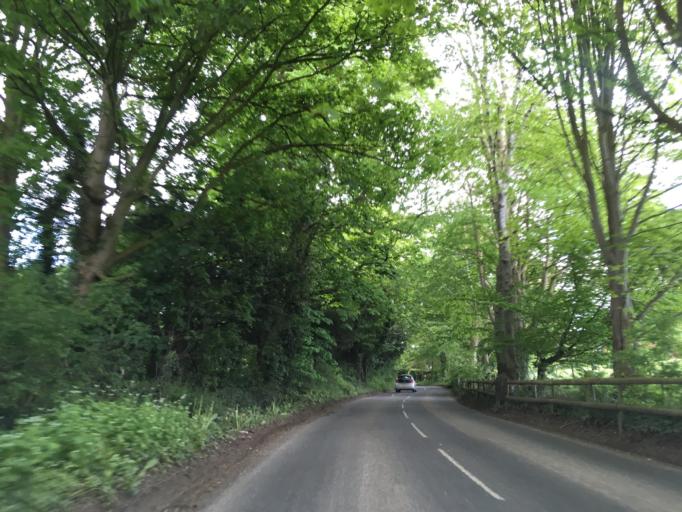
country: GB
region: England
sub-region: Gloucestershire
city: Stonehouse
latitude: 51.7266
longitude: -2.3095
